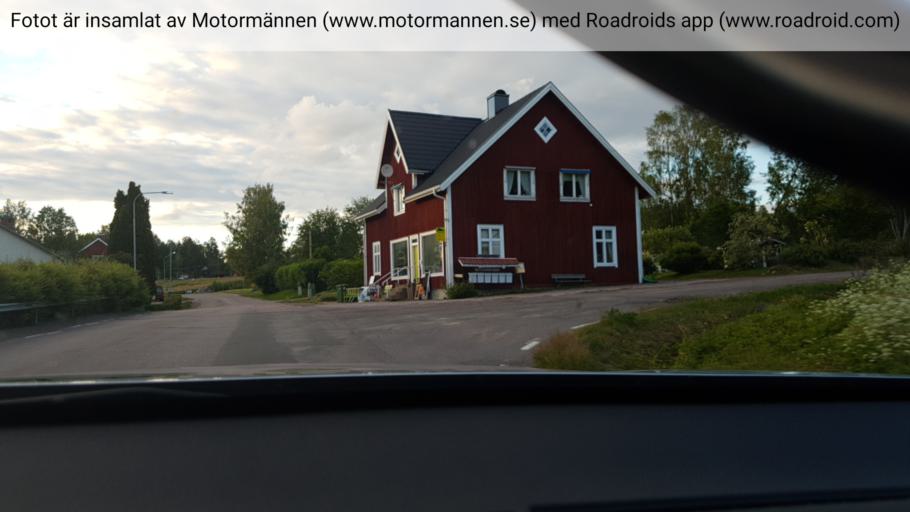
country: SE
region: Vaermland
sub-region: Torsby Kommun
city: Torsby
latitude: 60.1521
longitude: 13.0206
